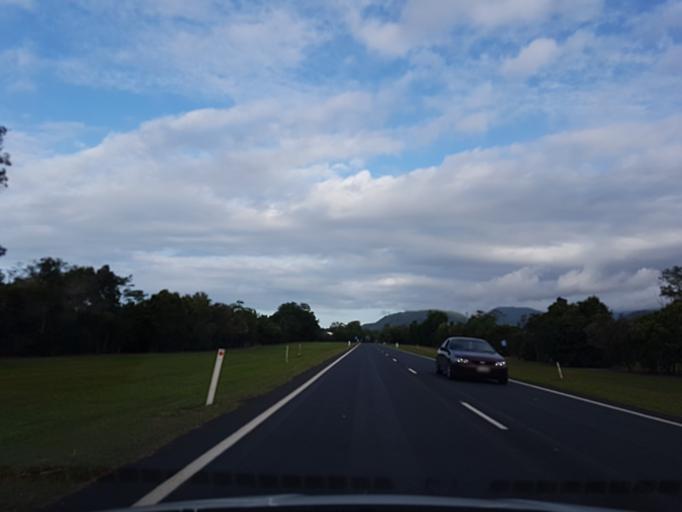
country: AU
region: Queensland
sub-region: Cairns
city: Port Douglas
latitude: -16.5311
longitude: 145.4641
